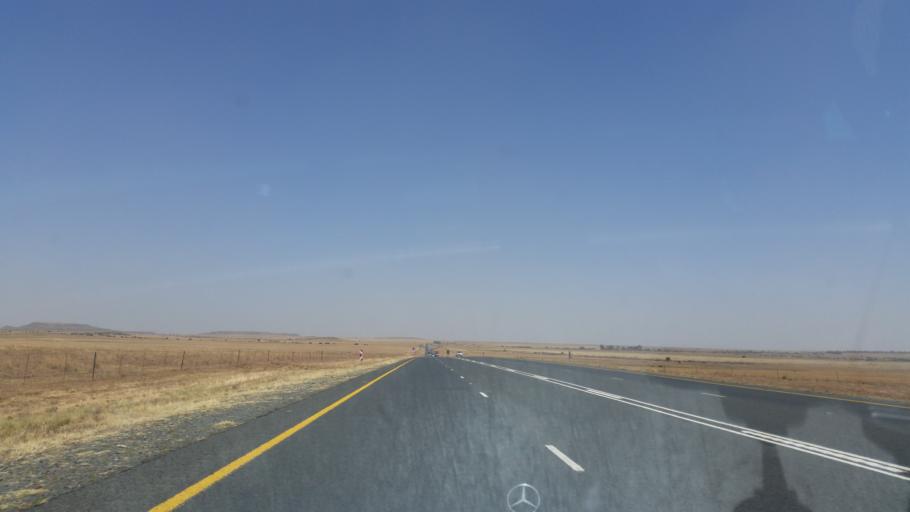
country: ZA
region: Orange Free State
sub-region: Lejweleputswa District Municipality
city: Brandfort
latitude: -28.7686
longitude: 26.7264
